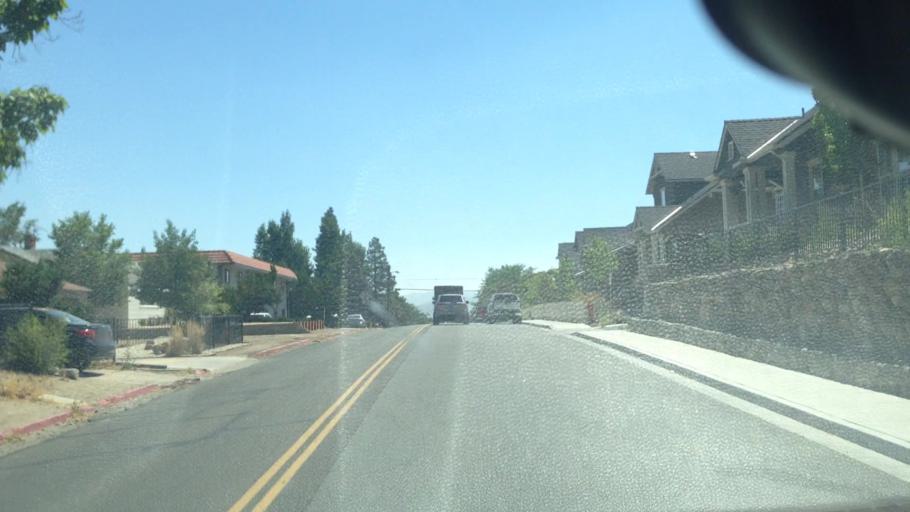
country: US
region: Nevada
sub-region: Washoe County
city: Reno
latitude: 39.5096
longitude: -119.8110
